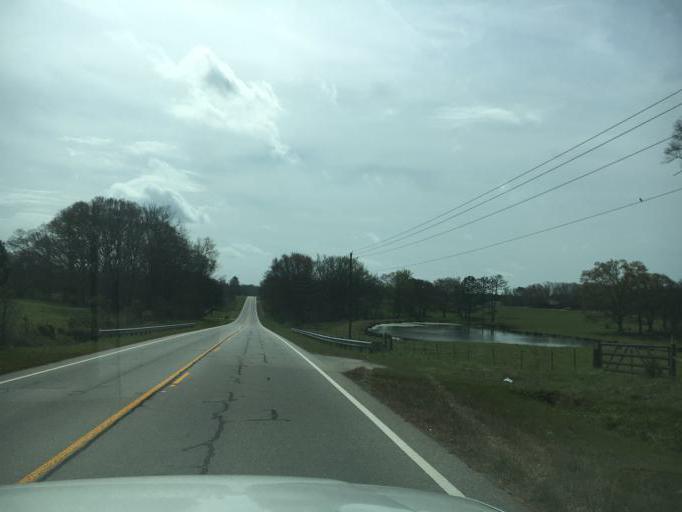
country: US
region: Georgia
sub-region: Franklin County
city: Gumlog
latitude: 34.4619
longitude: -83.0565
